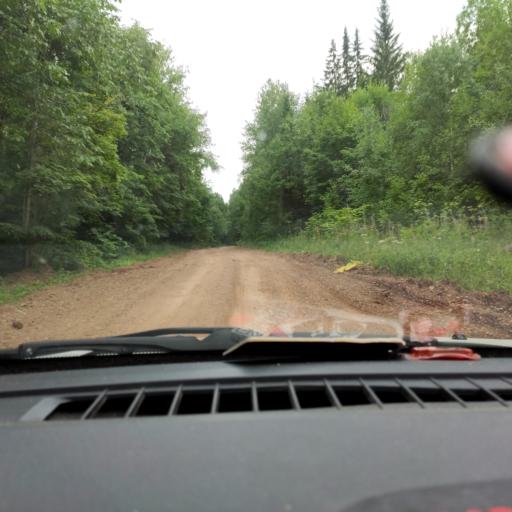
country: RU
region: Perm
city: Kultayevo
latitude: 57.8099
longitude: 56.0040
